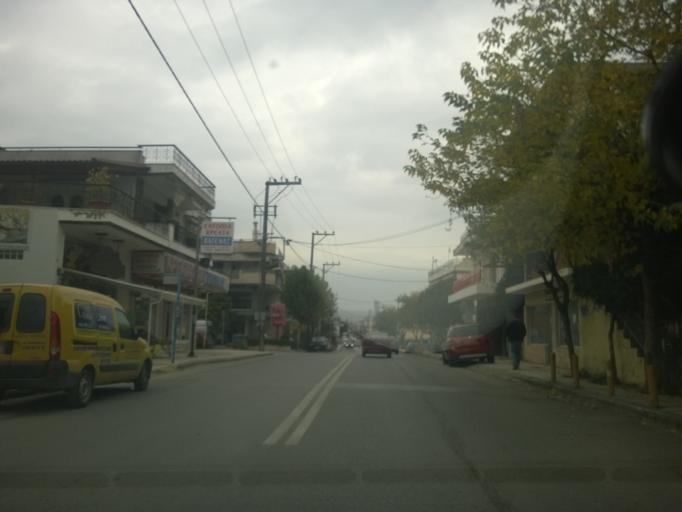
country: GR
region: Central Macedonia
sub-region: Nomos Thessalonikis
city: Stavroupoli
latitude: 40.6755
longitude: 22.9357
